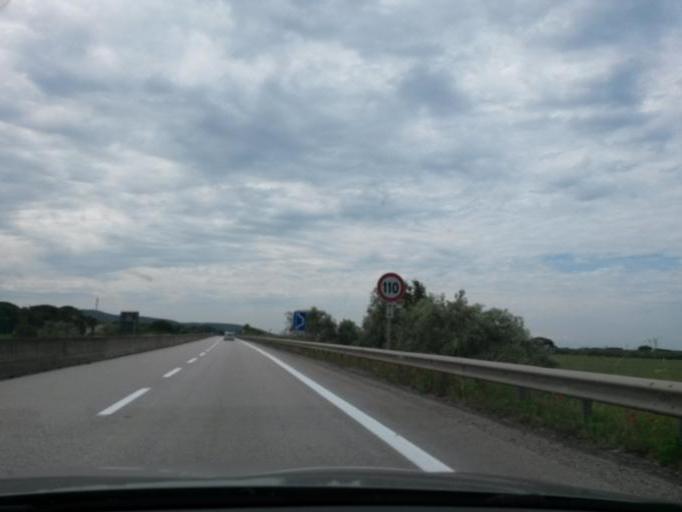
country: IT
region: Tuscany
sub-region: Provincia di Livorno
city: Donoratico
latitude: 43.1735
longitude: 10.5633
